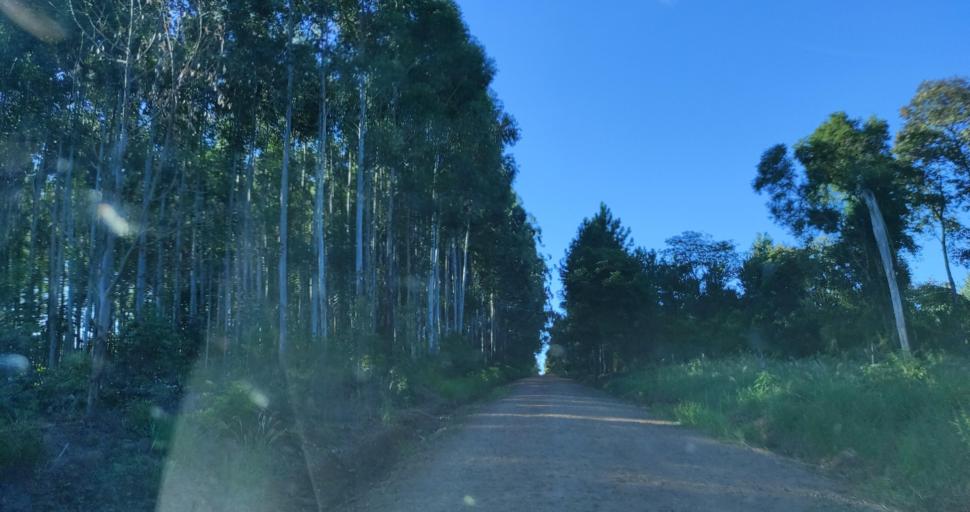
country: AR
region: Misiones
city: Garuhape
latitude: -26.8611
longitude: -55.0044
